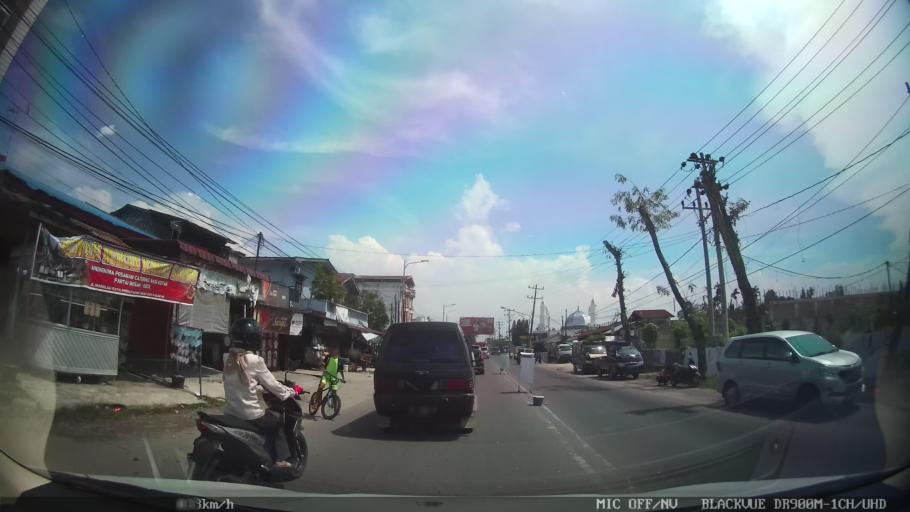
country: ID
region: North Sumatra
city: Labuhan Deli
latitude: 3.6763
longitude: 98.6560
